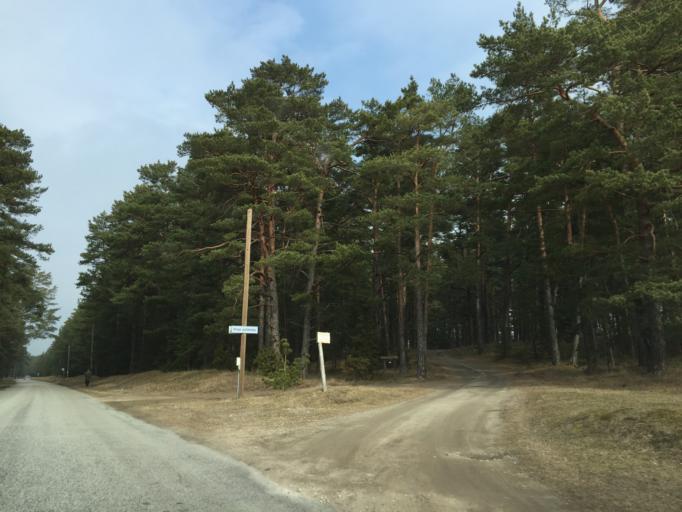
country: LV
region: Salacgrivas
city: Ainazi
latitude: 57.9271
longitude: 24.3912
